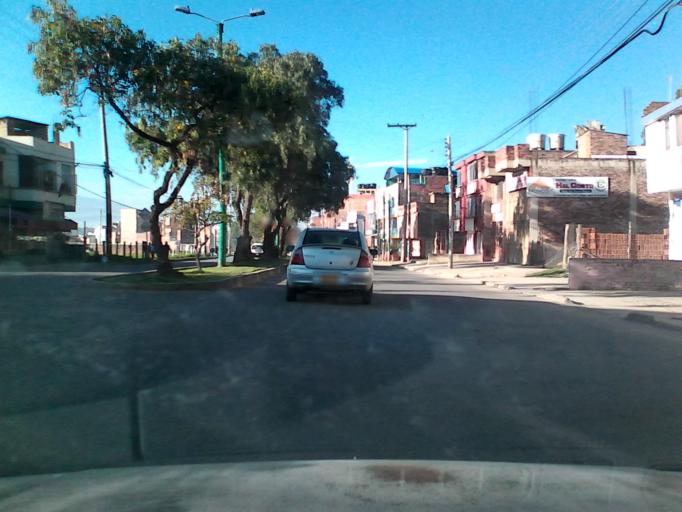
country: CO
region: Boyaca
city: Duitama
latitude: 5.8222
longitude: -73.0278
